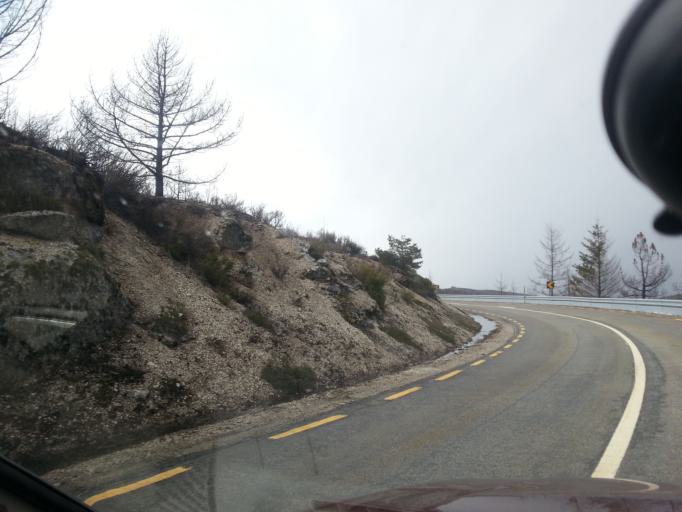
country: PT
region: Guarda
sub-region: Manteigas
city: Manteigas
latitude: 40.4153
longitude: -7.5819
